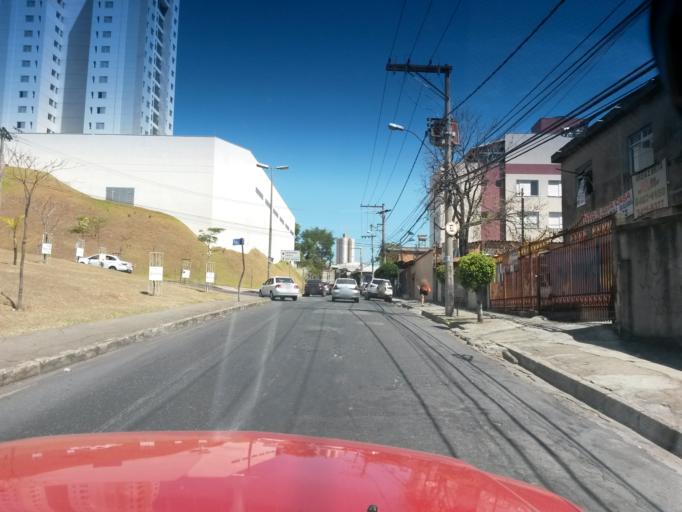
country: BR
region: Minas Gerais
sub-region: Belo Horizonte
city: Belo Horizonte
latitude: -19.8919
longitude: -43.9690
